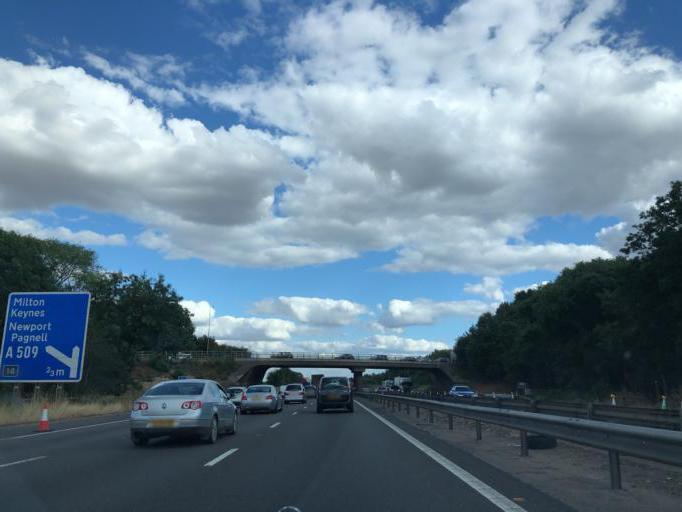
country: GB
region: England
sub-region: Milton Keynes
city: Newport Pagnell
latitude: 52.0688
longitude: -0.7221
